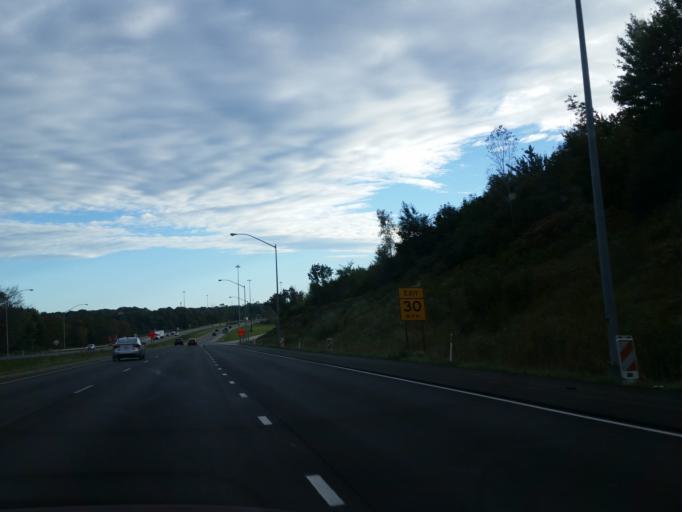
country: US
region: Pennsylvania
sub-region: Erie County
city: Wesleyville
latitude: 42.0889
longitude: -80.0127
